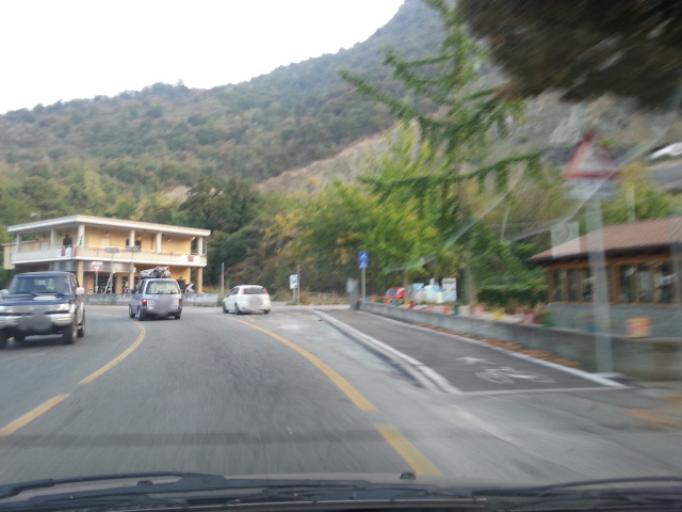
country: IT
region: Piedmont
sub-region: Provincia di Torino
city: Trana
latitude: 45.0350
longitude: 7.4199
